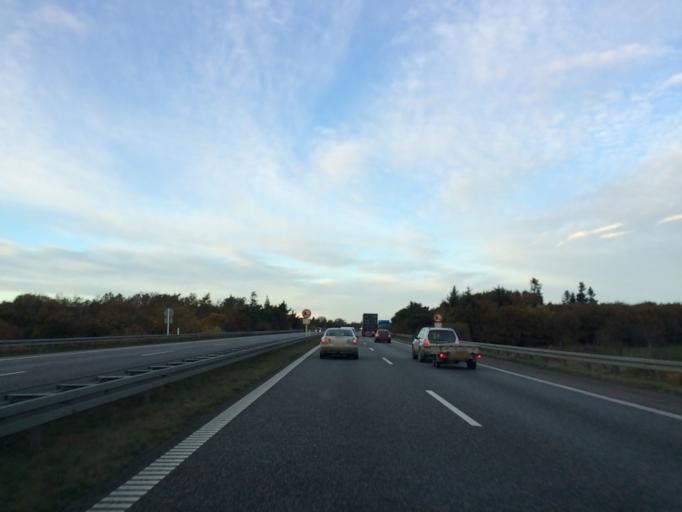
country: DK
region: South Denmark
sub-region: Aabenraa Kommune
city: Rodekro
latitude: 55.1546
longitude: 9.3721
